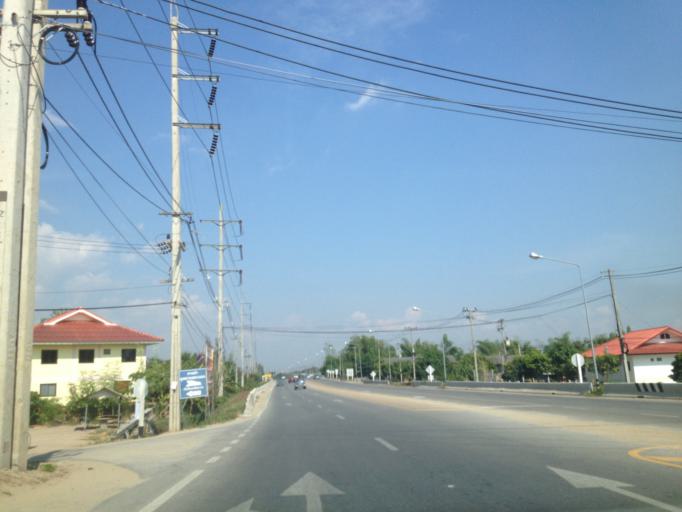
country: TH
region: Chiang Mai
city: Chom Thong
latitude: 18.3851
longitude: 98.6784
